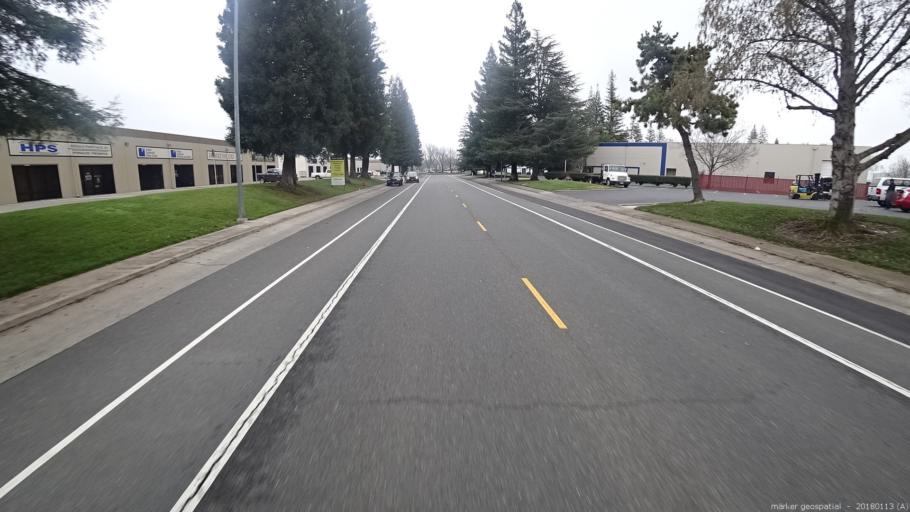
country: US
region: California
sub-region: Sacramento County
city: Gold River
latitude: 38.6068
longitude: -121.2627
